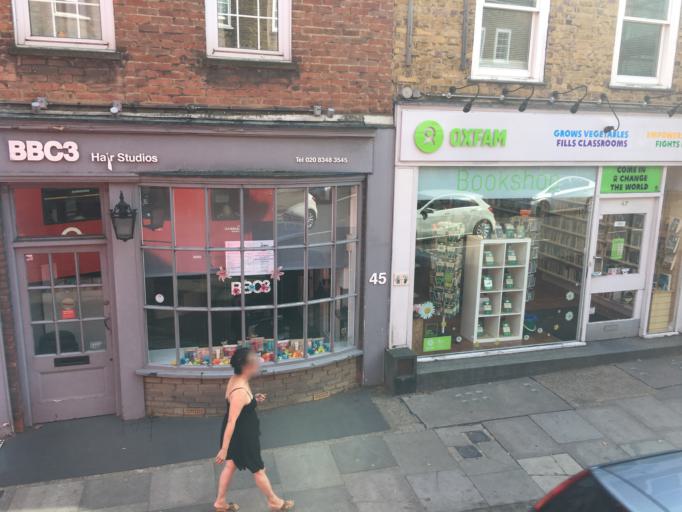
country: GB
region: England
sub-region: Greater London
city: Crouch End
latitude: 51.5709
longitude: -0.1485
